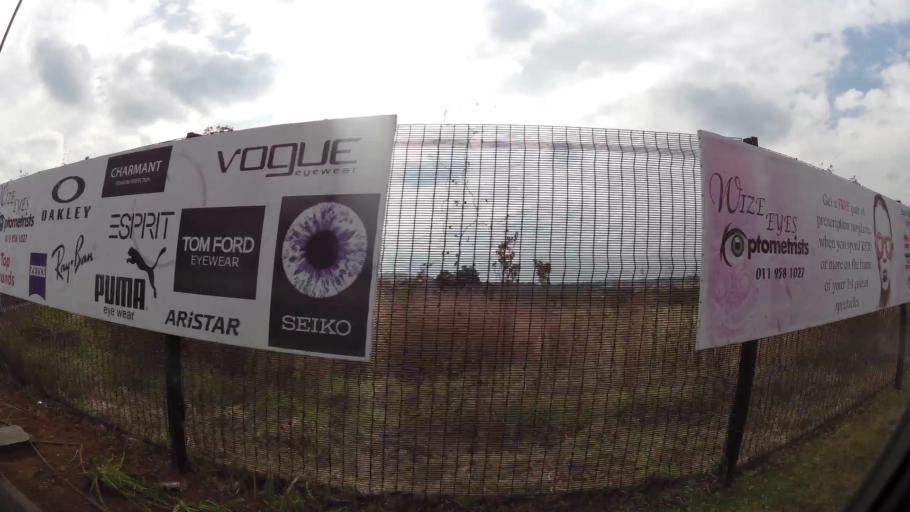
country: ZA
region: Gauteng
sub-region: City of Johannesburg Metropolitan Municipality
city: Roodepoort
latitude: -26.1082
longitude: 27.8853
